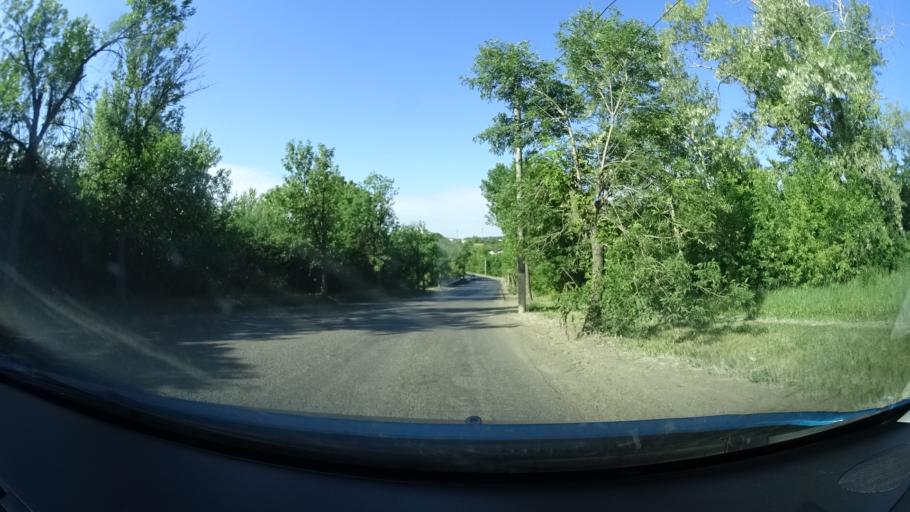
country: RU
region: Bashkortostan
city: Ufa
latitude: 54.8342
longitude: 56.0754
